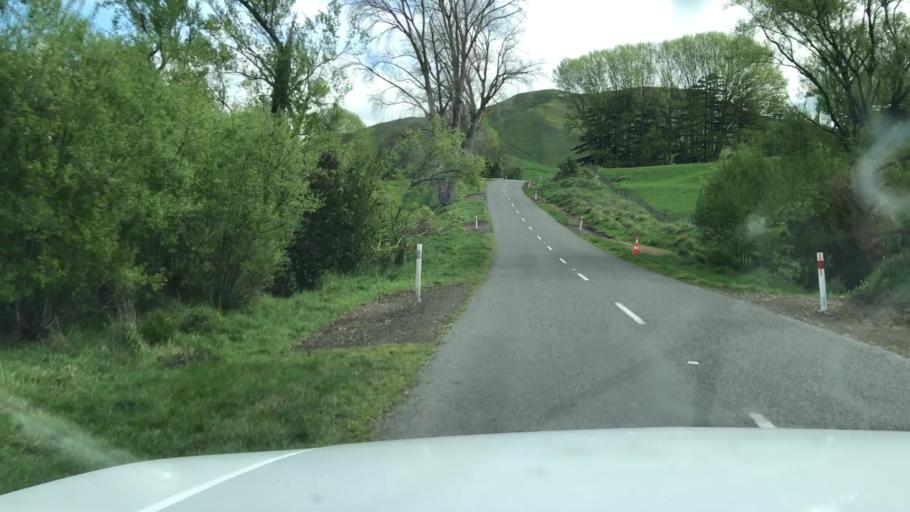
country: NZ
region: Hawke's Bay
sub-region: Hastings District
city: Hastings
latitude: -39.8199
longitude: 176.7393
